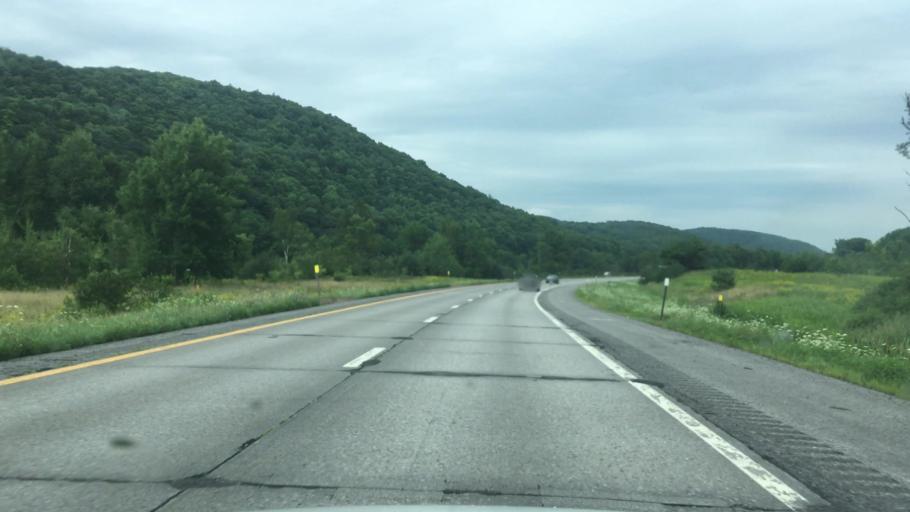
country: US
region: New York
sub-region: Otsego County
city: Worcester
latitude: 42.6016
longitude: -74.6988
